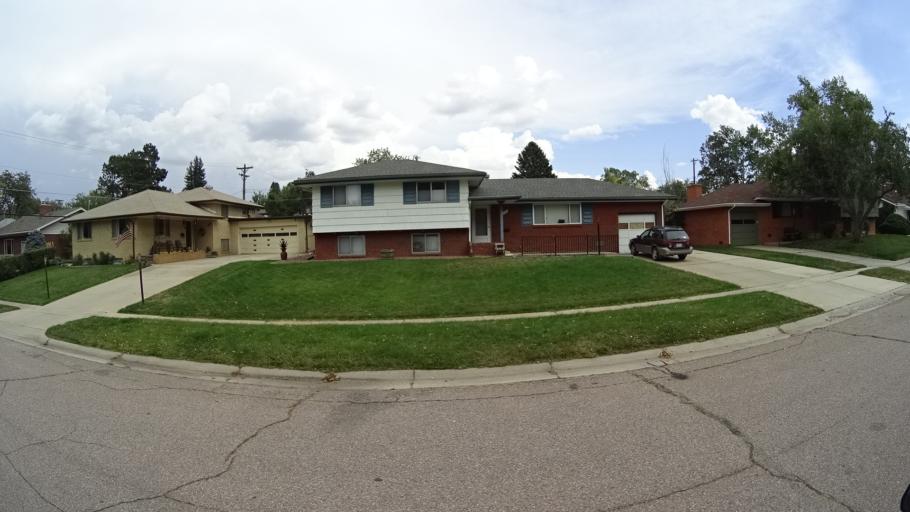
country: US
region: Colorado
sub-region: El Paso County
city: Colorado Springs
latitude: 38.8650
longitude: -104.7827
